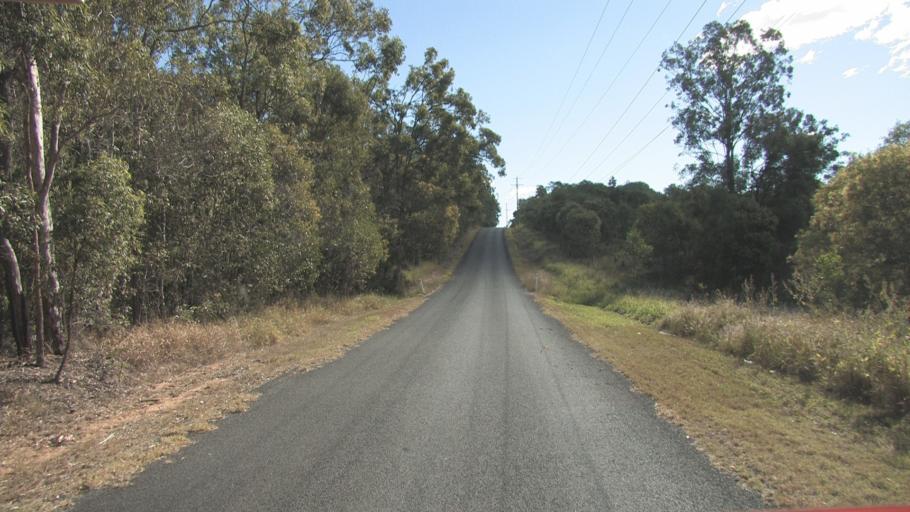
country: AU
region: Queensland
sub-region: Ipswich
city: Springfield Lakes
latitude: -27.7363
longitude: 152.9356
